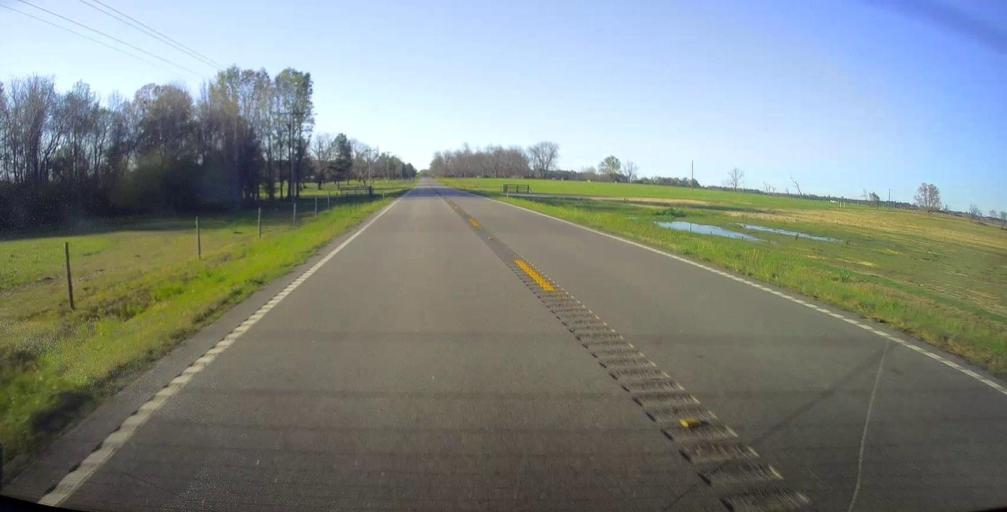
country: US
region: Georgia
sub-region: Wilcox County
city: Abbeville
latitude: 32.1497
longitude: -83.3485
